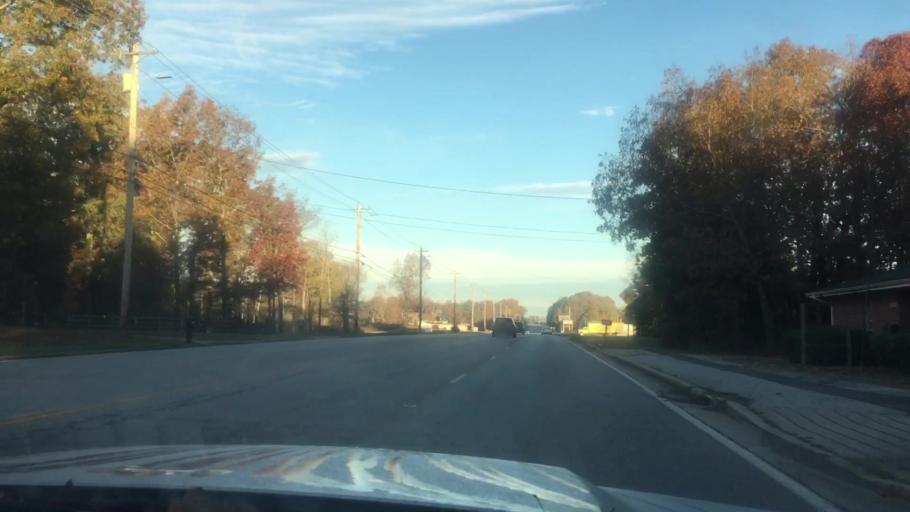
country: US
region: Tennessee
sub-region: Coffee County
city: Tullahoma
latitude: 35.3355
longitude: -86.1858
